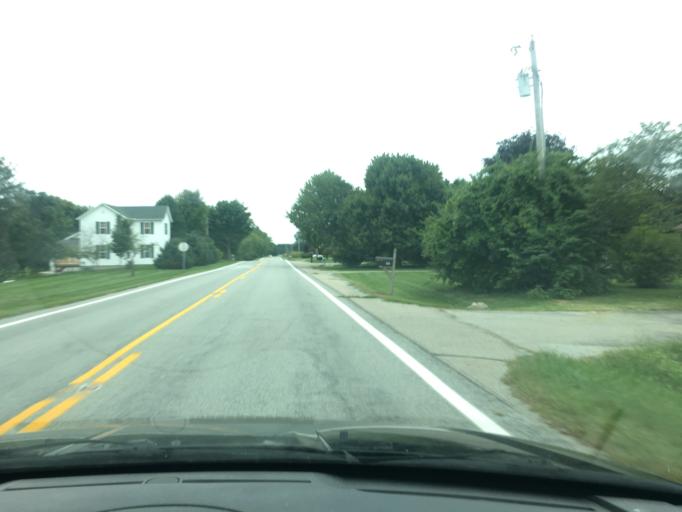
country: US
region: Ohio
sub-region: Champaign County
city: Urbana
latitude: 40.1567
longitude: -83.7697
